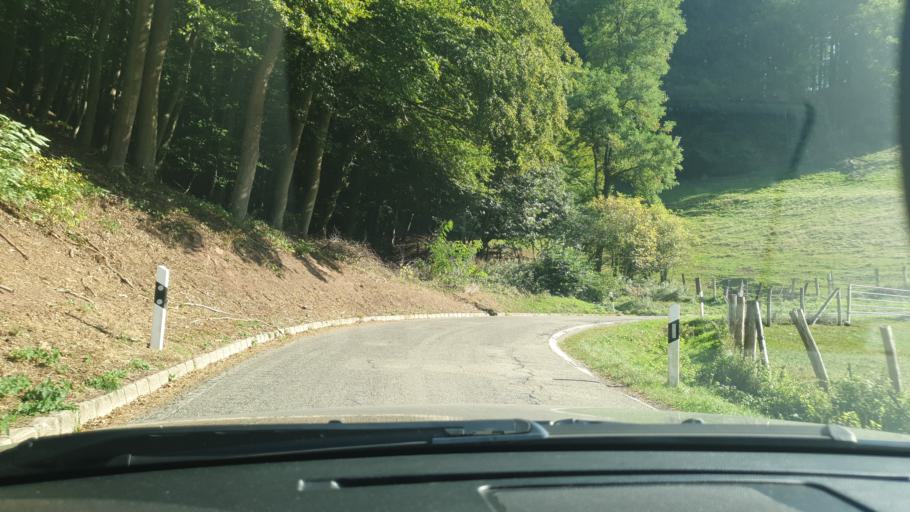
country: DE
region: Rheinland-Pfalz
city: Battweiler
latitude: 49.2925
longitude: 7.4640
